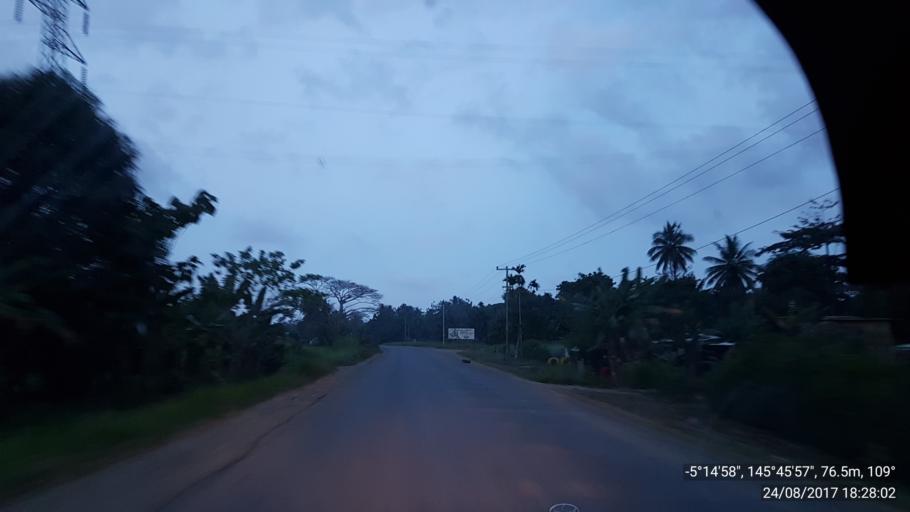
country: PG
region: Madang
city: Madang
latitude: -5.2497
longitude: 145.7658
